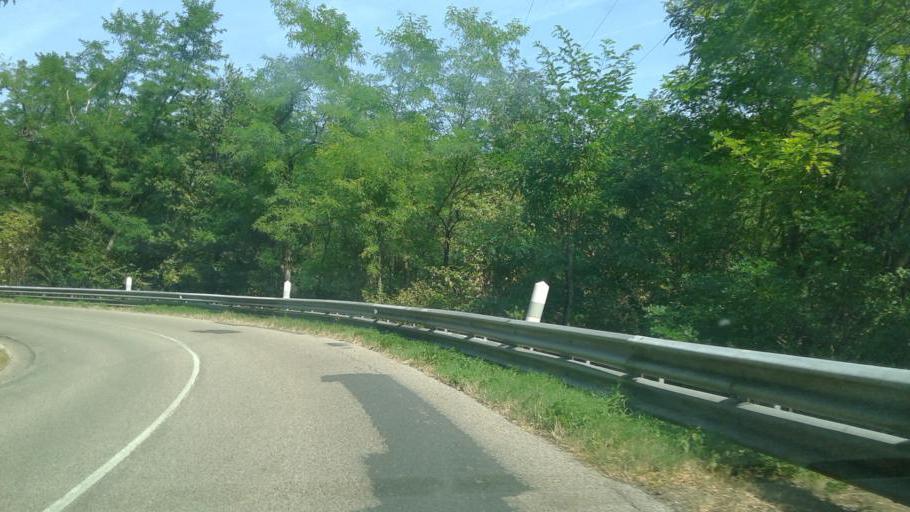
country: FR
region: Rhone-Alpes
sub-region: Departement de l'Ain
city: La Boisse
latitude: 45.8506
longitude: 5.0266
